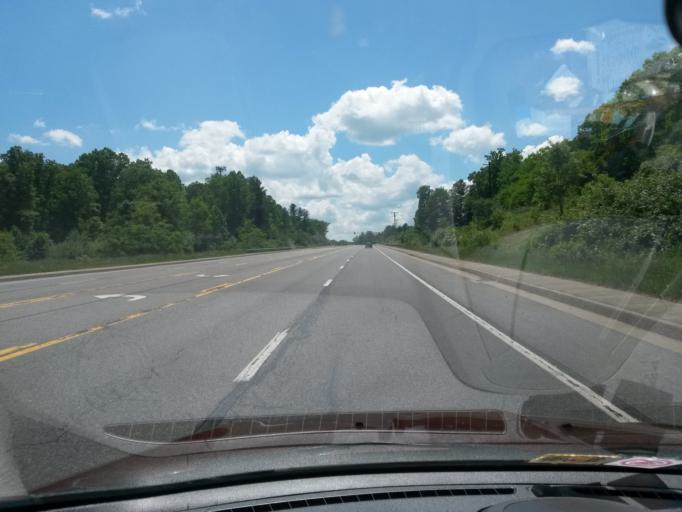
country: US
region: West Virginia
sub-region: Raleigh County
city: Beaver
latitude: 37.7807
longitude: -81.1534
